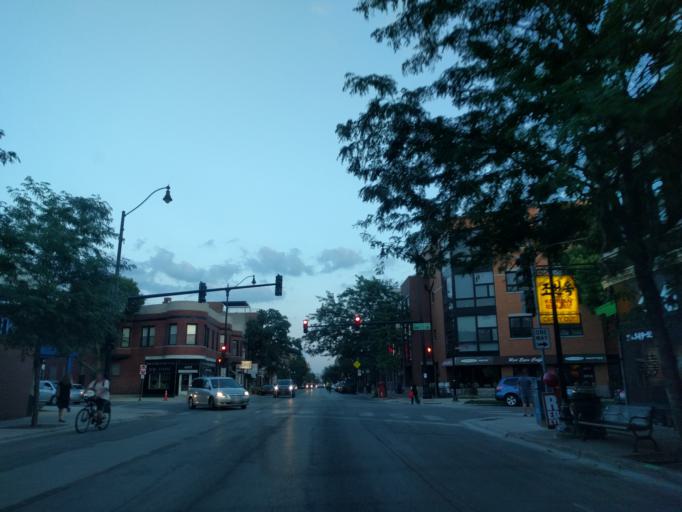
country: US
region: Illinois
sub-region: Cook County
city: Lincolnwood
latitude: 41.9580
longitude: -87.6815
